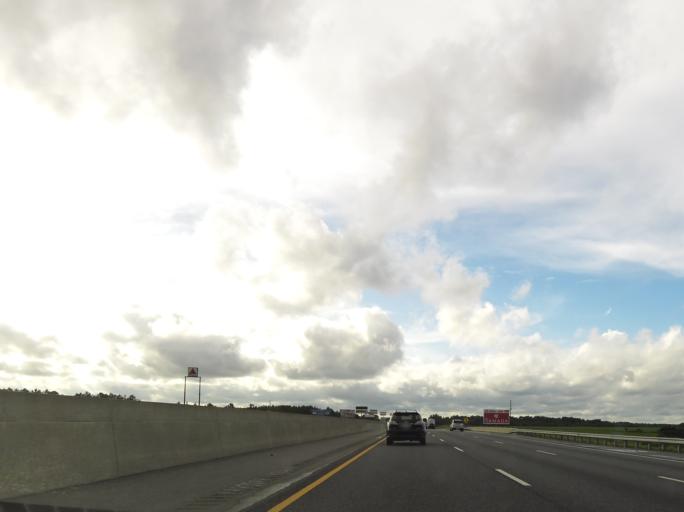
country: US
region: Georgia
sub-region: Turner County
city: Ashburn
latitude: 31.6800
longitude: -83.6191
